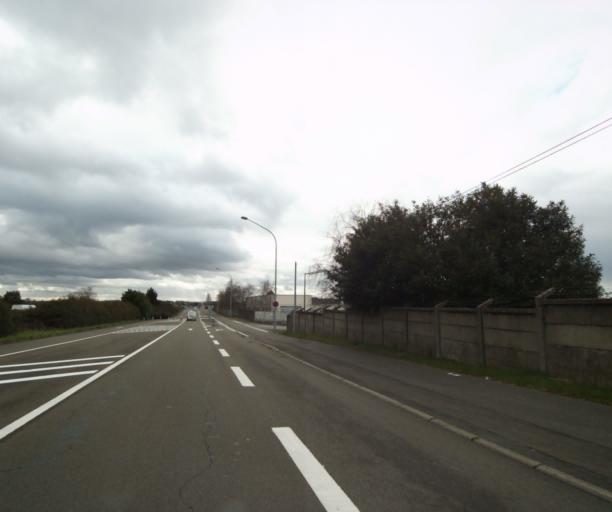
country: FR
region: Pays de la Loire
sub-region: Departement de la Sarthe
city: Arnage
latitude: 47.9555
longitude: 0.1976
